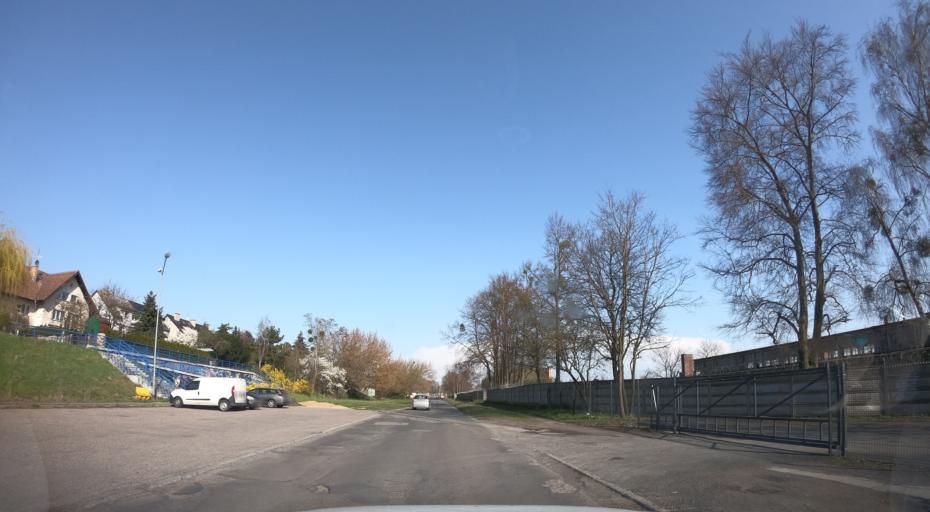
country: PL
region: West Pomeranian Voivodeship
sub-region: Szczecin
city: Szczecin
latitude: 53.4252
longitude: 14.5041
